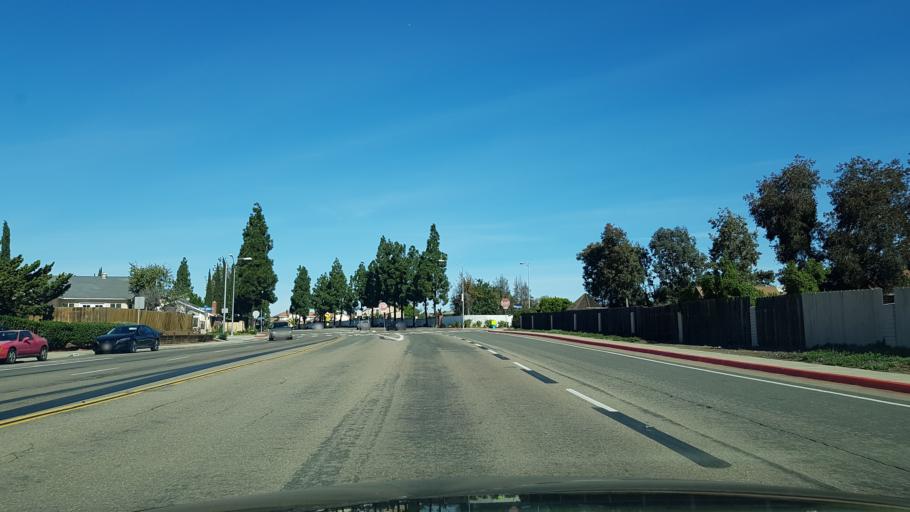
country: US
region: California
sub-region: San Diego County
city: Fairbanks Ranch
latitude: 32.9298
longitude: -117.1440
